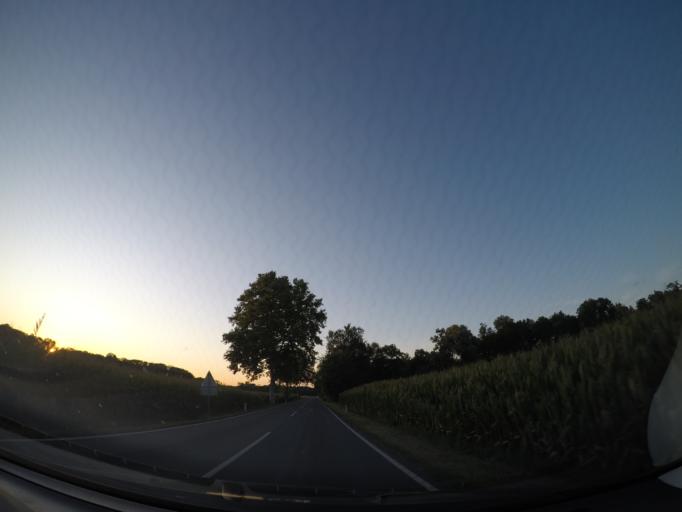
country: AT
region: Lower Austria
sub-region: Politischer Bezirk Baden
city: Seibersdorf
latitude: 47.9536
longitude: 16.5384
